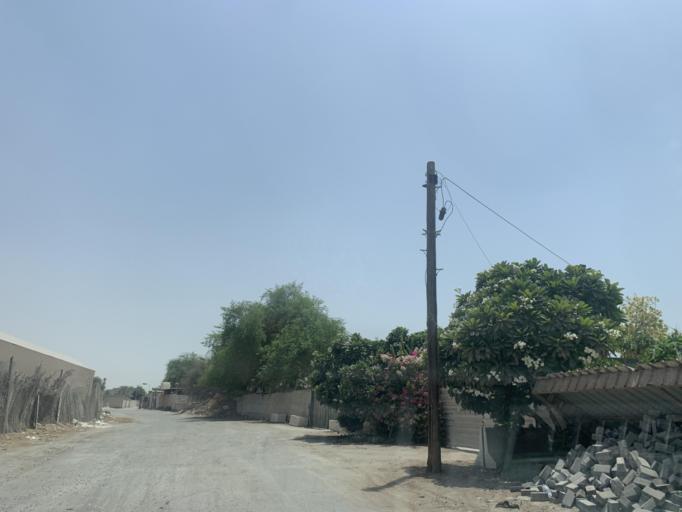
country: BH
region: Central Governorate
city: Madinat Hamad
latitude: 26.1572
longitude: 50.4956
